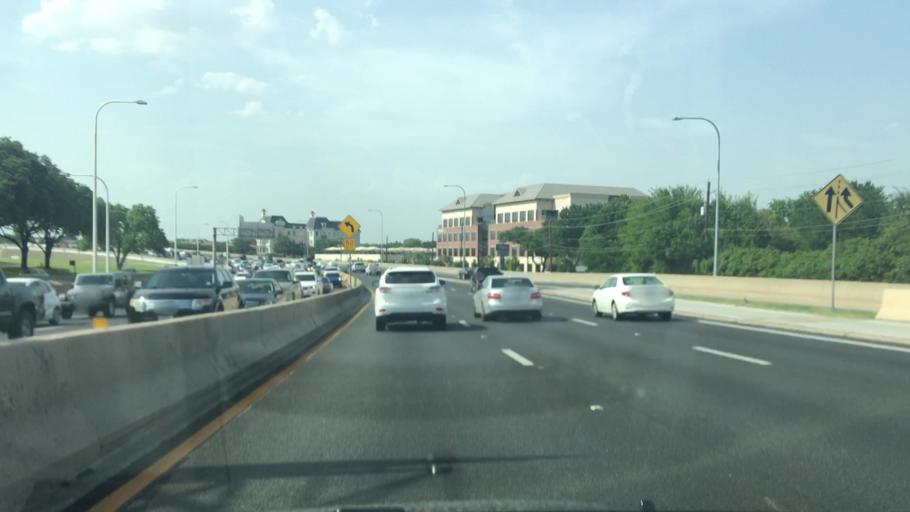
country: US
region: Texas
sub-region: Dallas County
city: Addison
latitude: 32.9711
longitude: -96.8214
